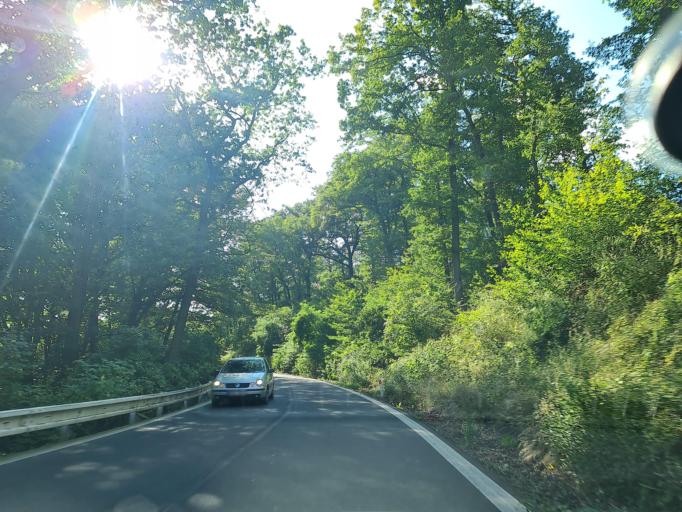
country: CZ
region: Ustecky
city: Mezibori
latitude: 50.6000
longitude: 13.5953
